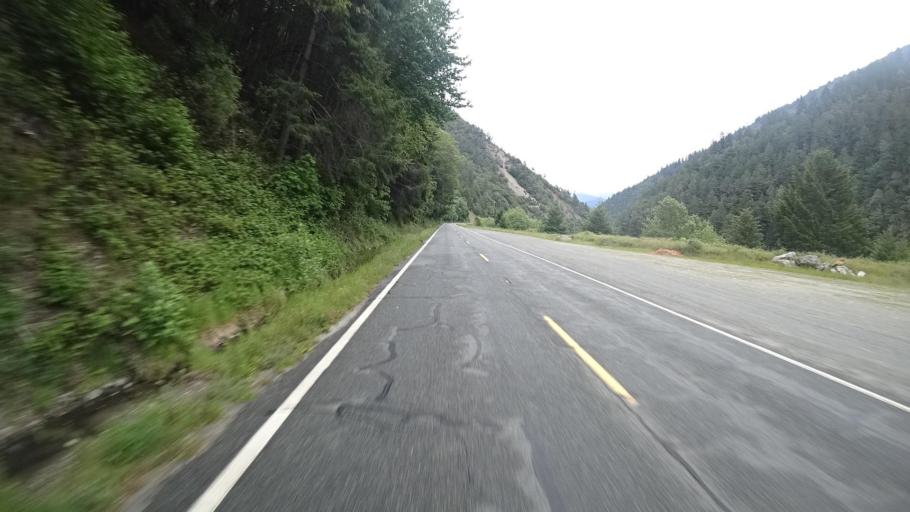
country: US
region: California
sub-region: Humboldt County
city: Willow Creek
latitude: 41.2541
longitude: -123.6338
